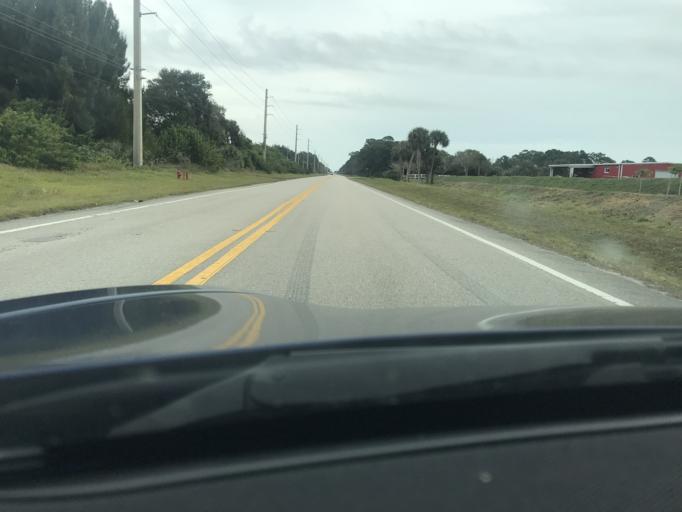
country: US
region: Florida
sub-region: Indian River County
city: Winter Beach
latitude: 27.7338
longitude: -80.4588
